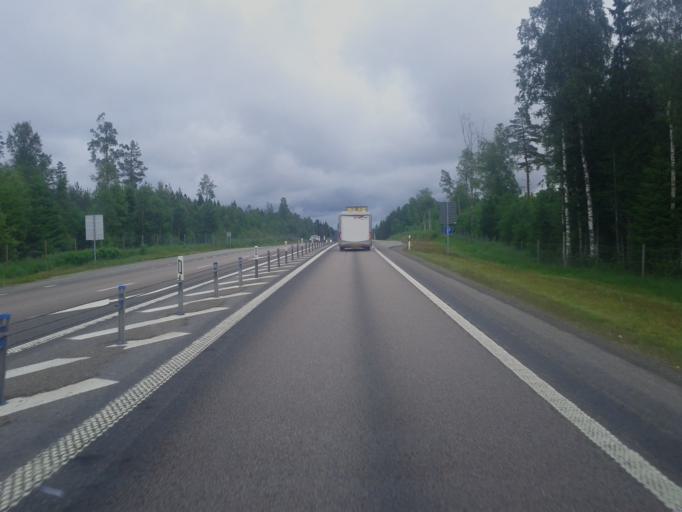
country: SE
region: Vaesternorrland
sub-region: Haernoesands Kommun
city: Haernoesand
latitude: 62.5683
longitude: 17.7382
